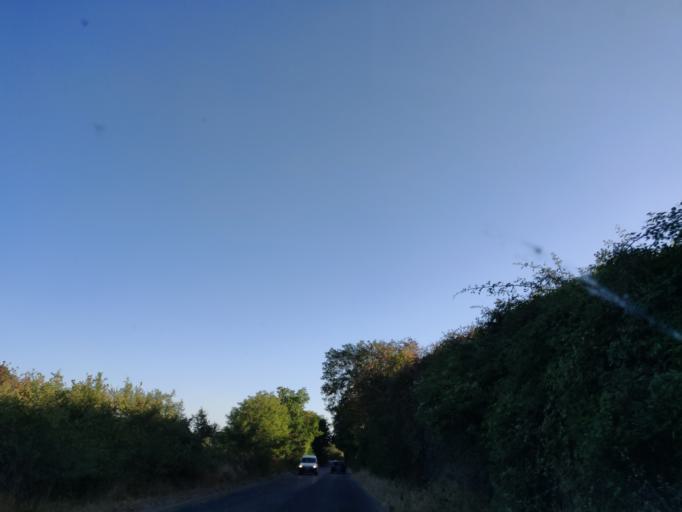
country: IT
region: Latium
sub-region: Provincia di Viterbo
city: Grotte di Castro
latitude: 42.6891
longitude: 11.8754
